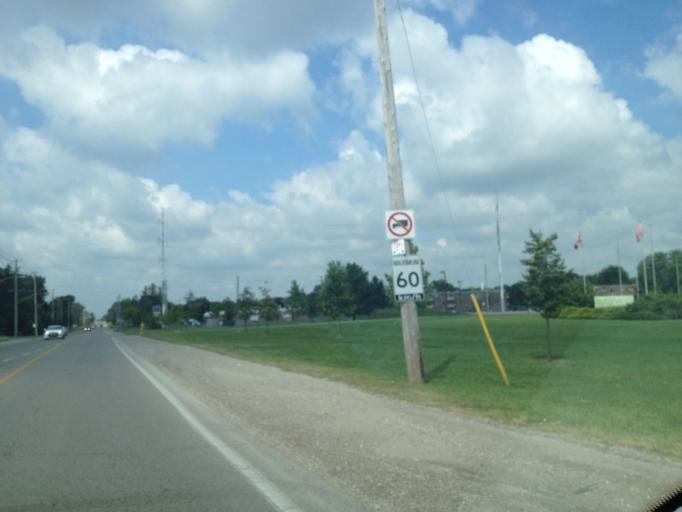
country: CA
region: Ontario
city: London
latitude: 43.0277
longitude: -81.1885
